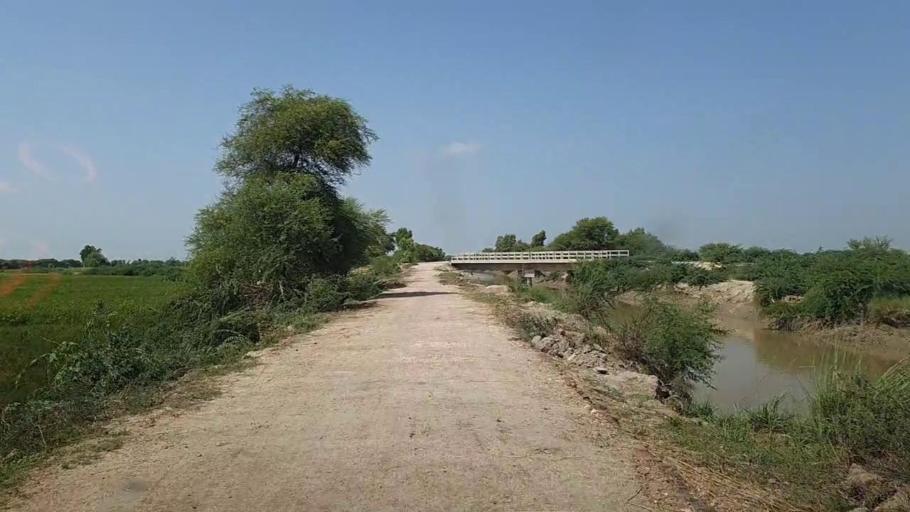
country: PK
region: Sindh
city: Kario
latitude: 24.6615
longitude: 68.5479
